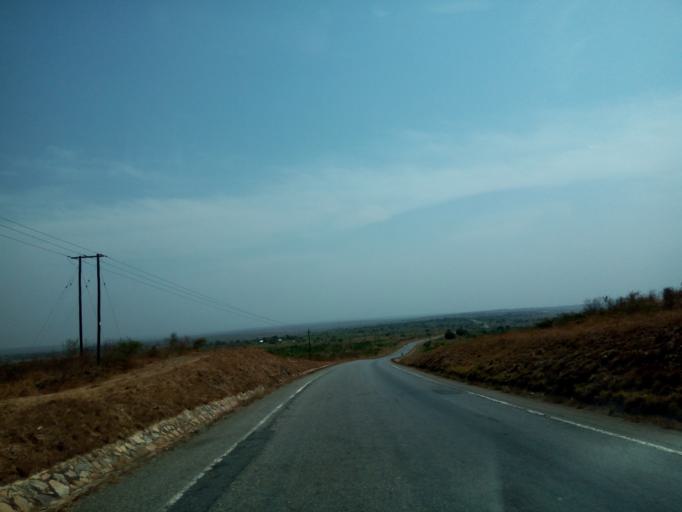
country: UG
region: Northern Region
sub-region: Nebbi District
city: Nebbi
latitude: 2.4624
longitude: 31.2940
